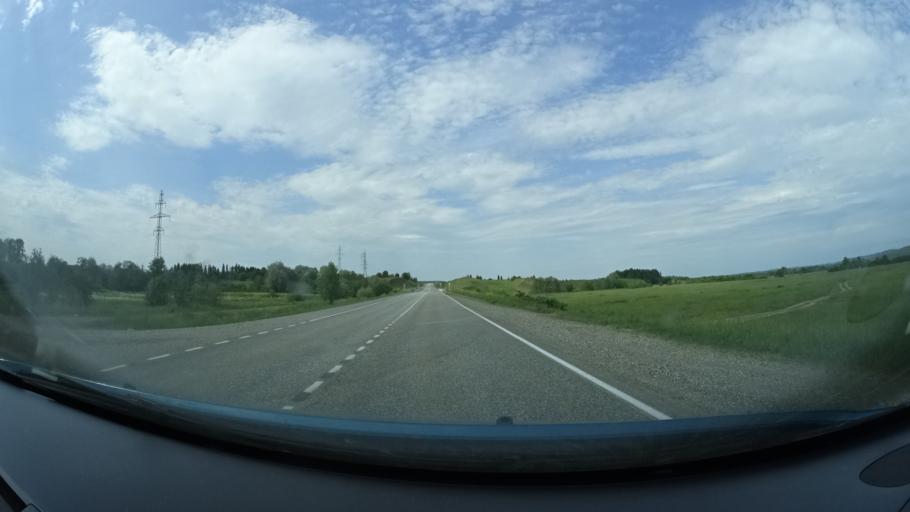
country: RU
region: Perm
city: Barda
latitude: 57.0894
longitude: 55.5380
